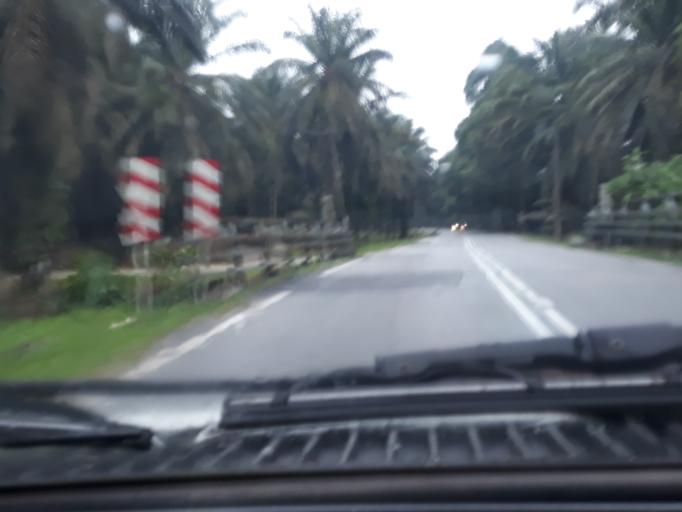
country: MY
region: Kedah
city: Kulim
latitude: 5.2406
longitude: 100.6013
